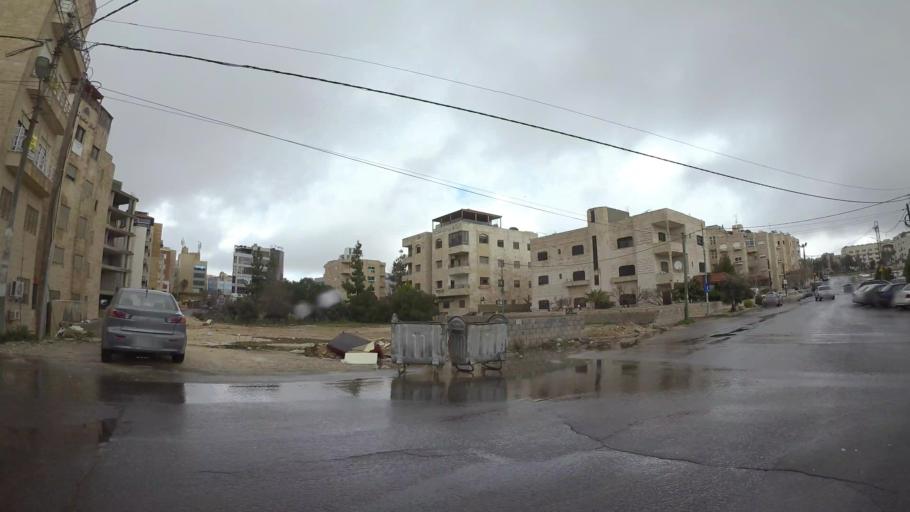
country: JO
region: Amman
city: Wadi as Sir
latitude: 31.9530
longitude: 35.8549
